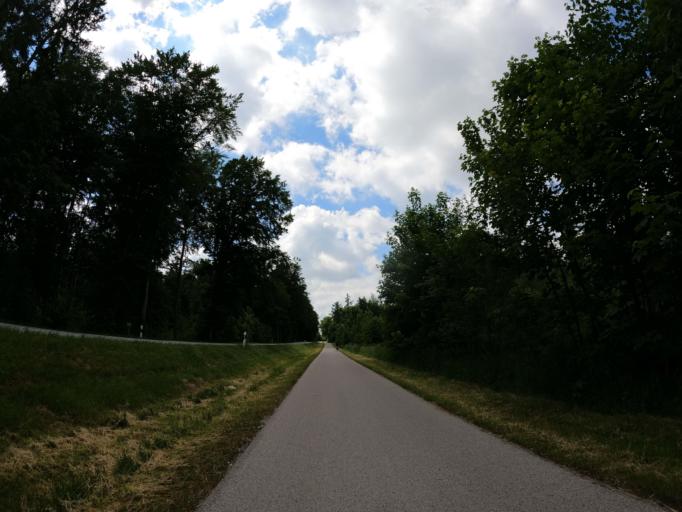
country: DE
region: Bavaria
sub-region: Upper Bavaria
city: Oberhaching
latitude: 48.0028
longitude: 11.5790
